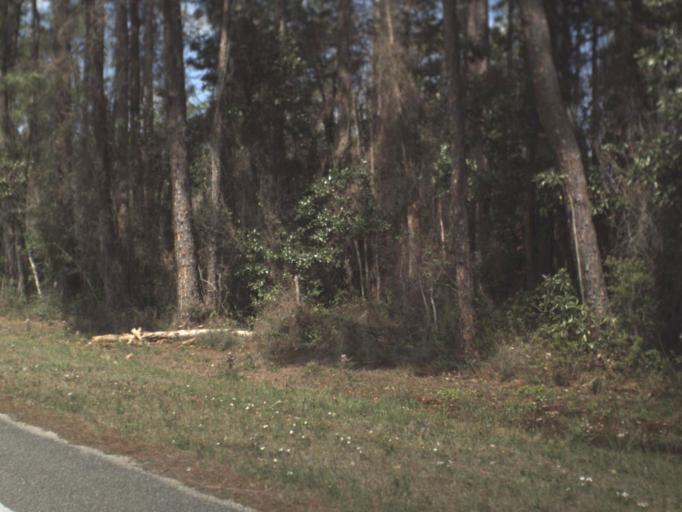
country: US
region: Florida
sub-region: Gulf County
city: Port Saint Joe
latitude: 29.7361
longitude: -85.1621
